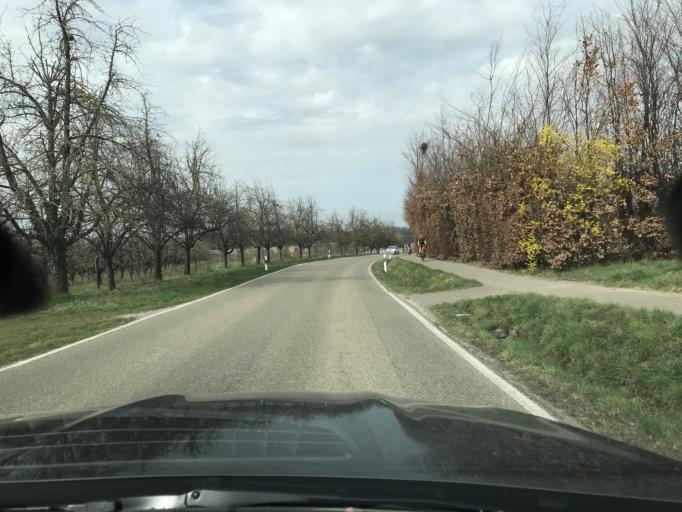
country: DE
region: Baden-Wuerttemberg
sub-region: Regierungsbezirk Stuttgart
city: Burgstetten
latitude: 48.9095
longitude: 9.3796
